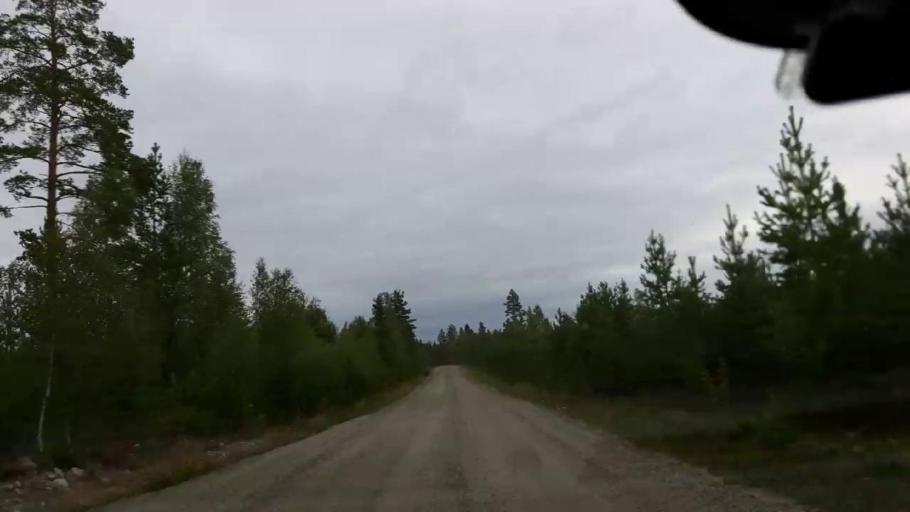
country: SE
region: Vaesternorrland
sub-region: Ange Kommun
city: Ange
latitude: 62.8134
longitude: 15.7197
